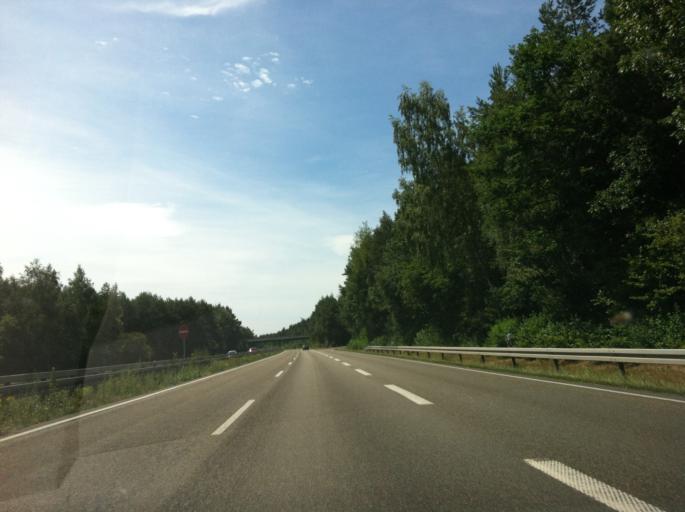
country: DE
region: Hesse
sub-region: Regierungsbezirk Darmstadt
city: Eppertshausen
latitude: 49.9849
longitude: 8.8727
